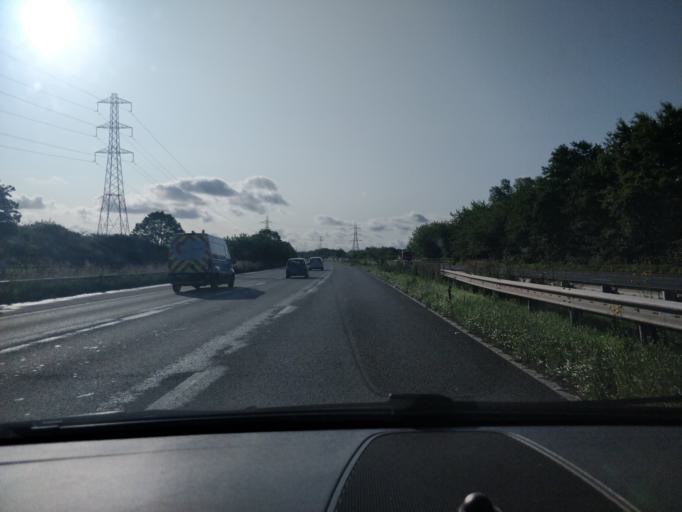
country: GB
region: England
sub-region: Sefton
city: Melling
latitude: 53.4868
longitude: -2.9347
